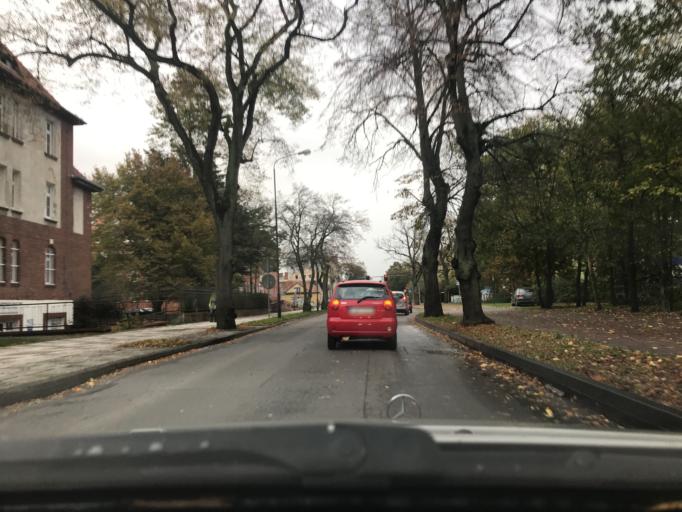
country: PL
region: West Pomeranian Voivodeship
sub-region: Swinoujscie
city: Swinoujscie
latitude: 53.9131
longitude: 14.2390
